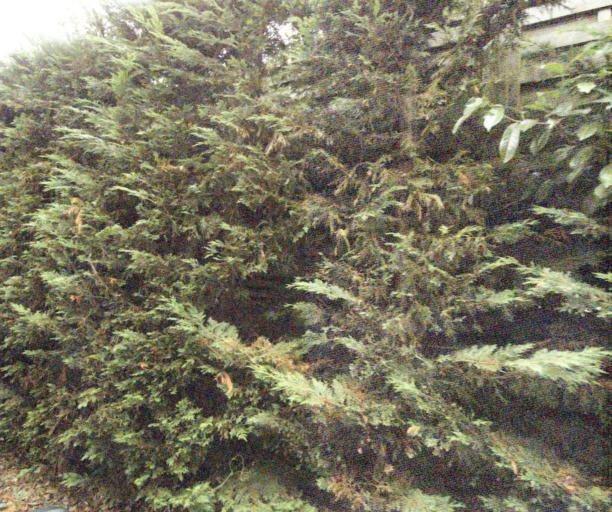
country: FR
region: Nord-Pas-de-Calais
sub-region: Departement du Nord
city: Ronchin
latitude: 50.5900
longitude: 3.0874
